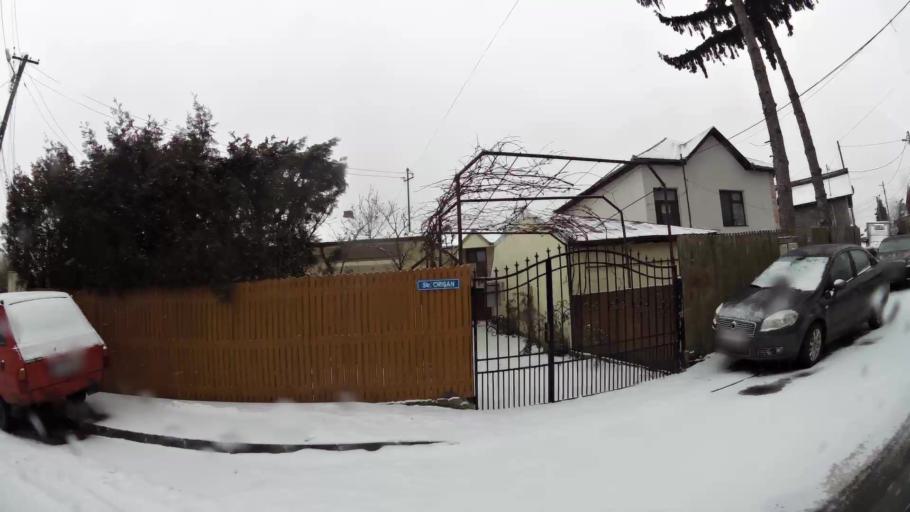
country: RO
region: Dambovita
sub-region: Municipiul Targoviste
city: Targoviste
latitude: 44.9237
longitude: 25.4760
